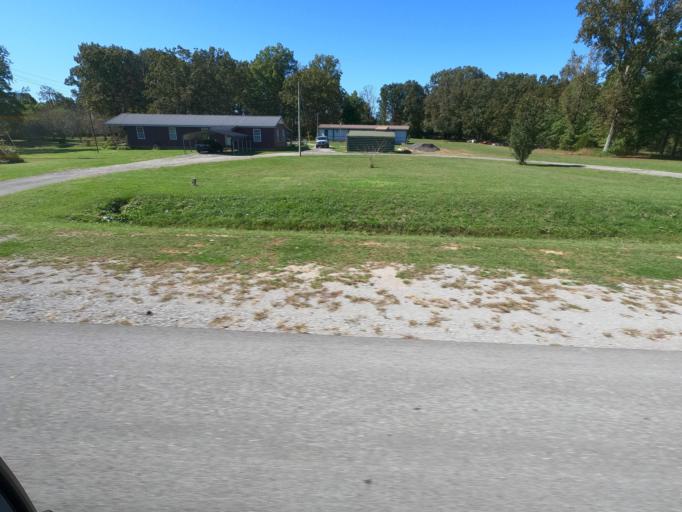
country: US
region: Tennessee
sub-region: Maury County
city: Mount Pleasant
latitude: 35.4351
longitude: -87.2805
